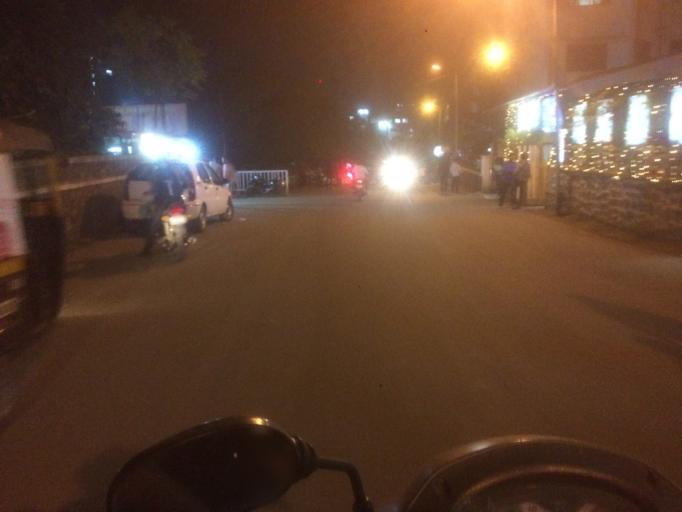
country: IN
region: Maharashtra
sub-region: Pune Division
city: Pune
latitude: 18.4633
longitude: 73.8366
